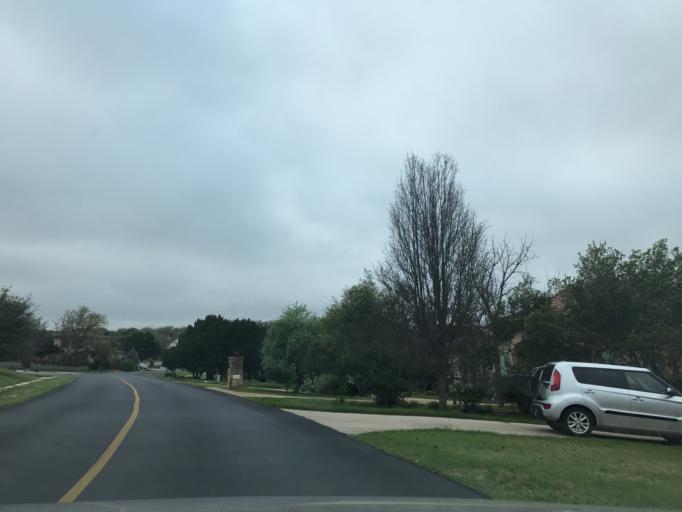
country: US
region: Texas
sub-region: Travis County
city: The Hills
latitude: 30.3418
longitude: -97.9923
